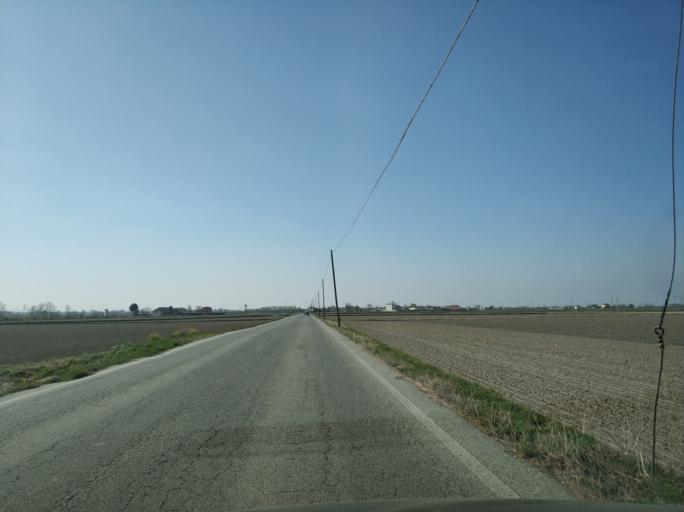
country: IT
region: Piedmont
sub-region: Provincia di Novara
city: Vinzaglio
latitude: 45.3173
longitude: 8.4908
